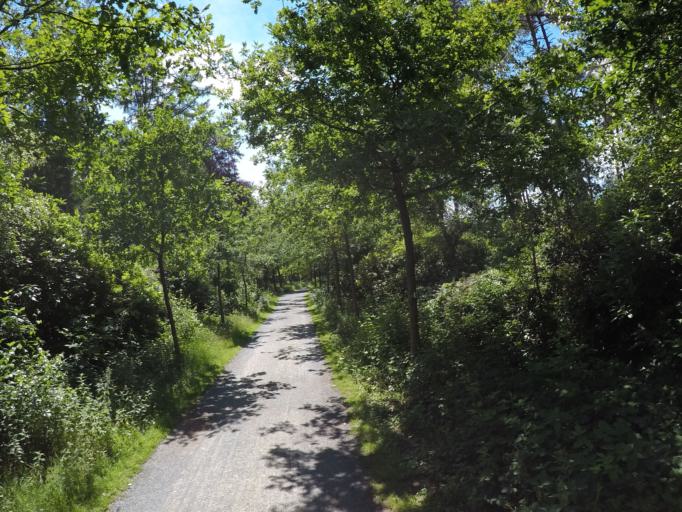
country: BE
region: Flanders
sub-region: Provincie Antwerpen
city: Vosselaar
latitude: 51.2906
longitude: 4.8874
